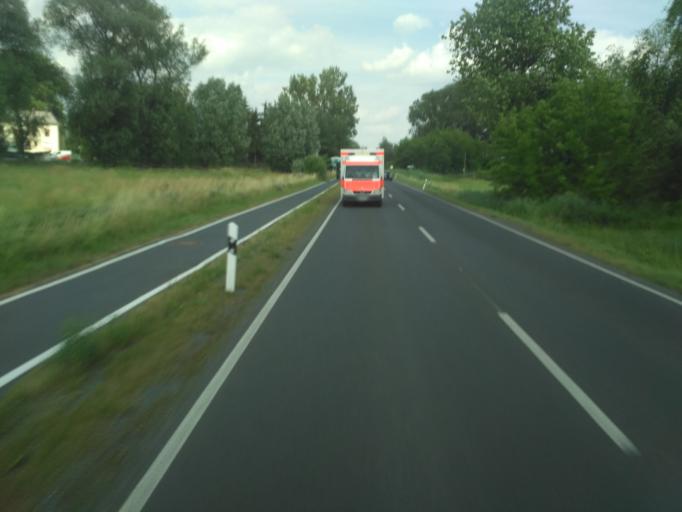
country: DE
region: Saxony
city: Niederau
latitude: 51.1693
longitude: 13.5130
